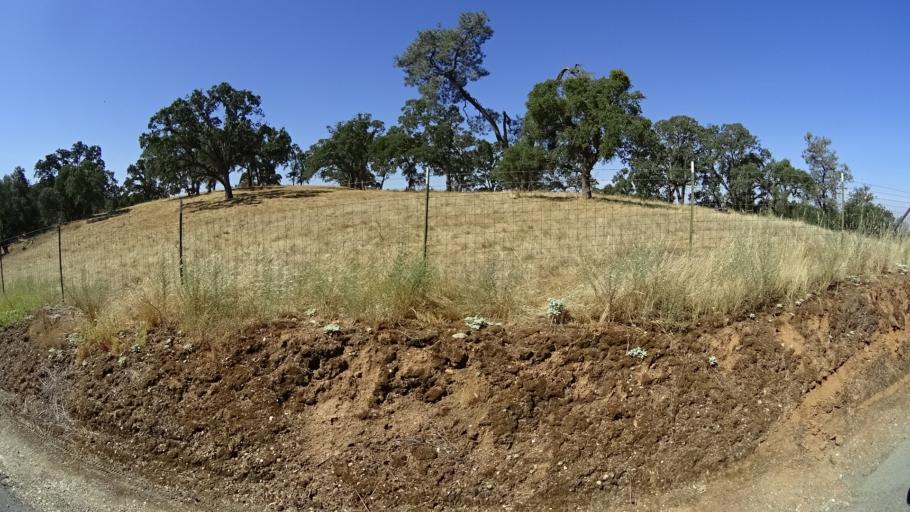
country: US
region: California
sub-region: Calaveras County
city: Valley Springs
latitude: 38.2285
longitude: -120.8591
